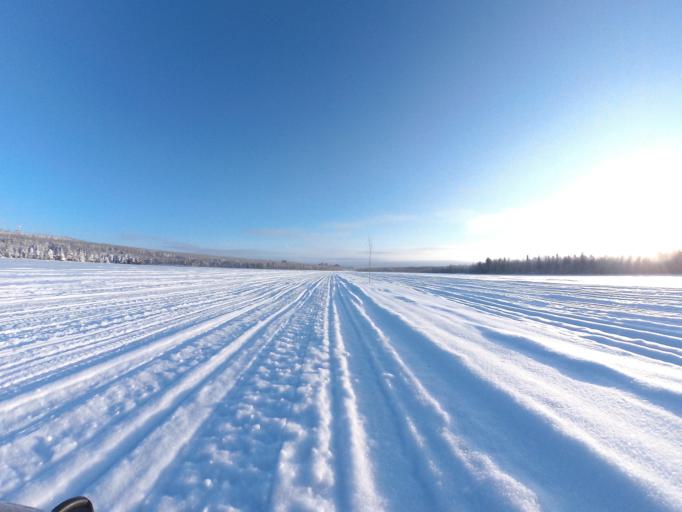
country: FI
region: Lapland
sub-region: Rovaniemi
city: Rovaniemi
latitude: 66.6026
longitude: 25.8231
